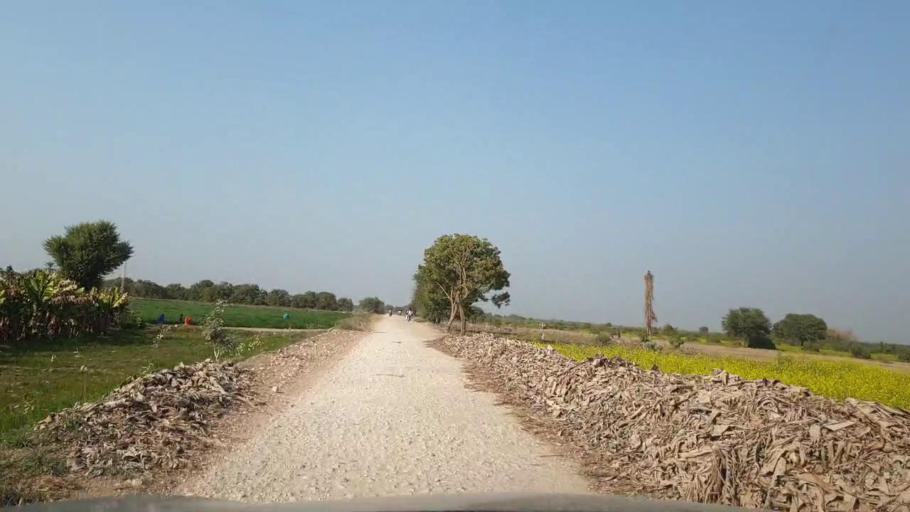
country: PK
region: Sindh
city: Tando Allahyar
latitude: 25.5726
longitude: 68.7951
